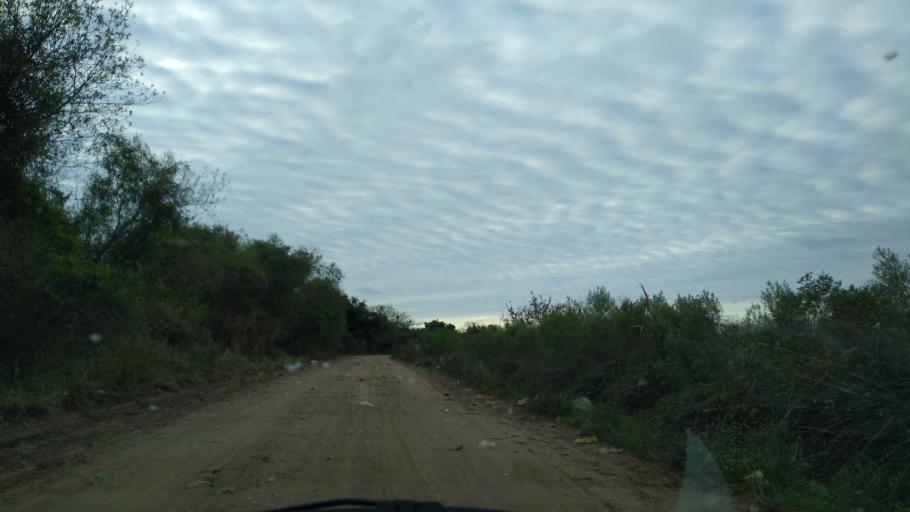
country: AR
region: Chaco
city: Fontana
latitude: -27.3960
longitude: -59.0487
